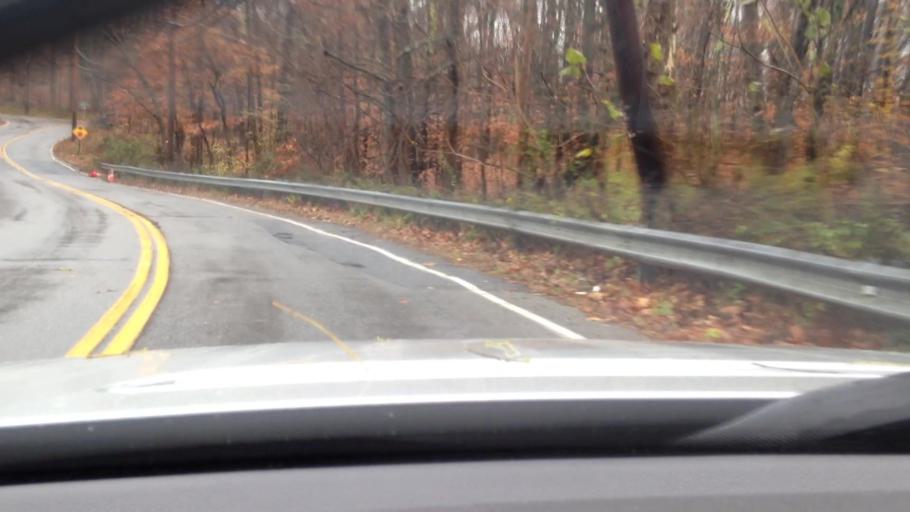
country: US
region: New York
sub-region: Westchester County
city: Crugers
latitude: 41.2351
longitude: -73.8977
